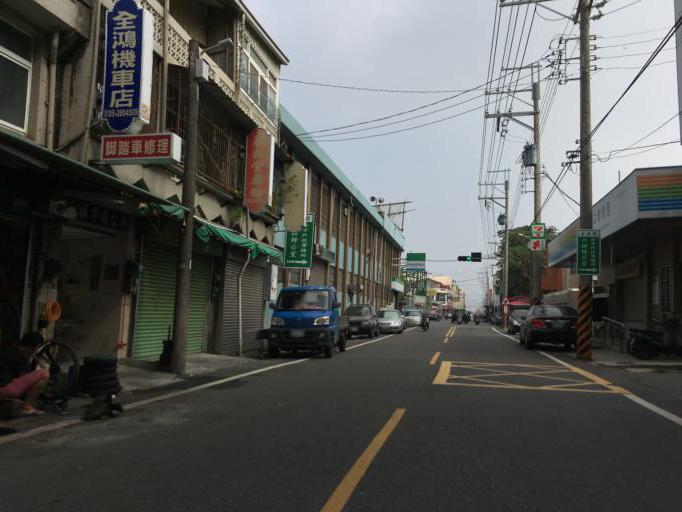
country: TW
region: Taiwan
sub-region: Chiayi
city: Taibao
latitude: 23.4921
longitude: 120.2920
